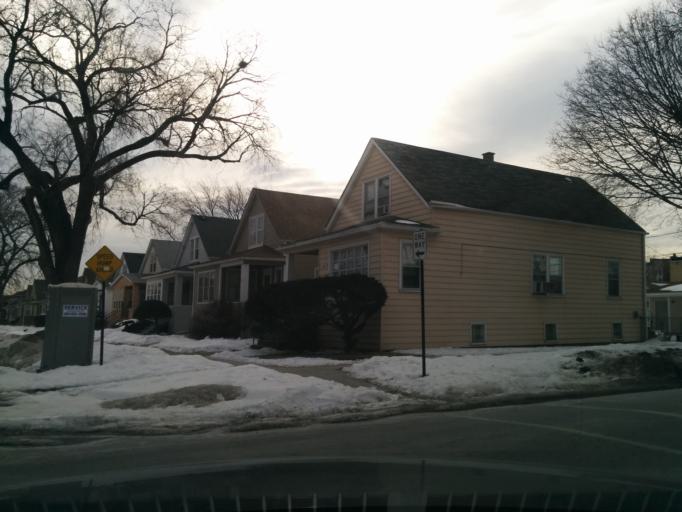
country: US
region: Illinois
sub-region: Cook County
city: Harwood Heights
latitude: 41.9478
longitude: -87.7521
